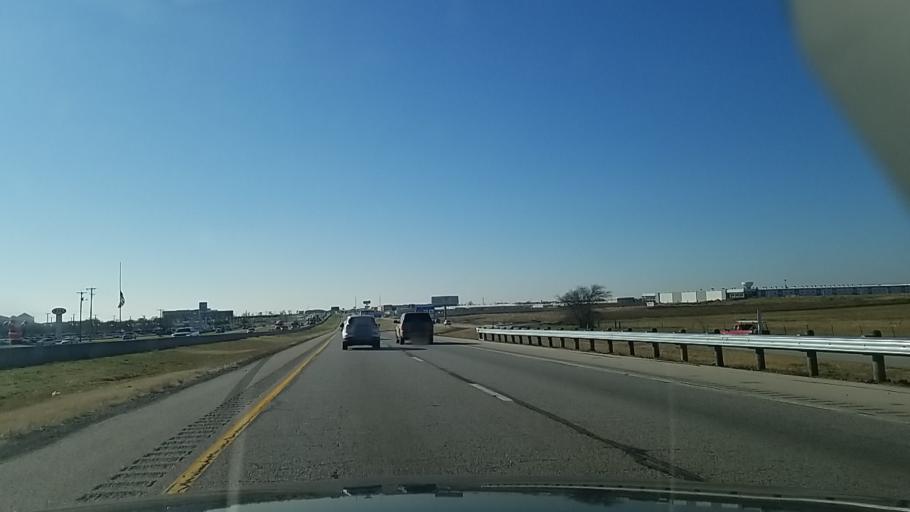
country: US
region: Texas
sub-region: Tarrant County
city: Haslet
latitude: 32.9408
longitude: -97.3132
